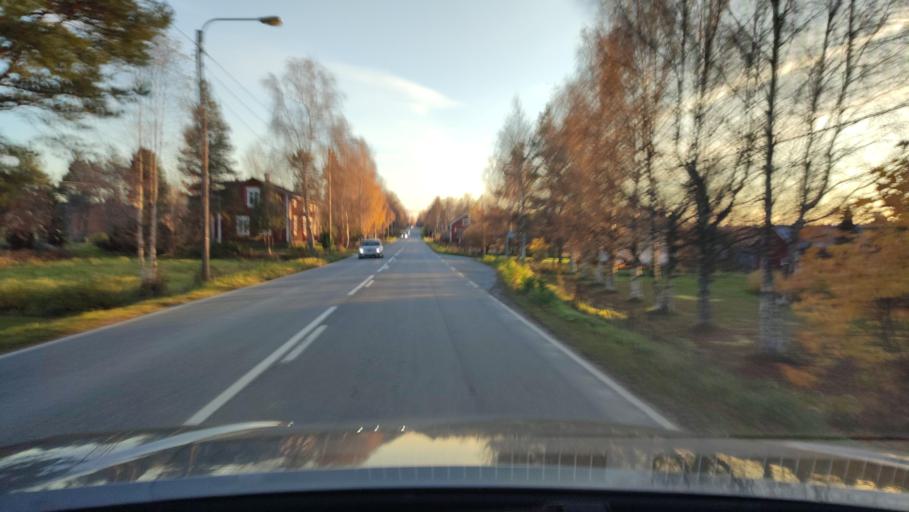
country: FI
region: Ostrobothnia
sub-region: Sydosterbotten
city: Naerpes
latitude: 62.4939
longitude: 21.3430
